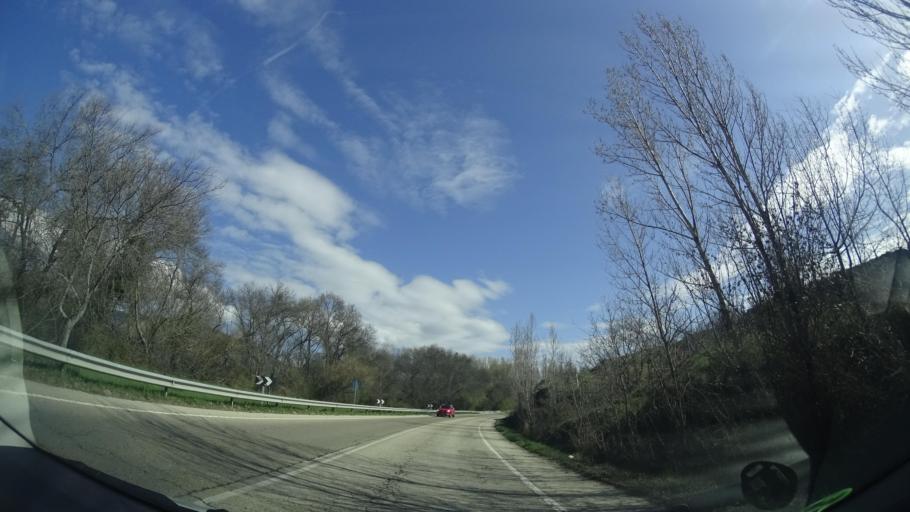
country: ES
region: Madrid
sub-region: Provincia de Madrid
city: Miraflores de la Sierra
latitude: 40.7415
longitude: -3.7862
